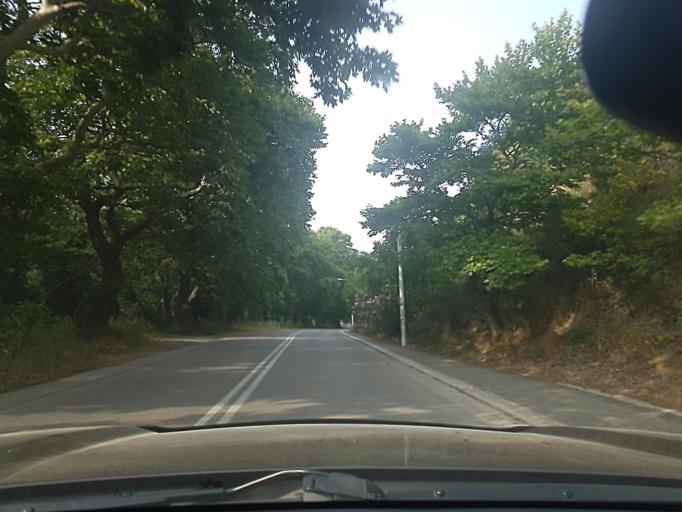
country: GR
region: Central Greece
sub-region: Nomos Evvoias
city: Yimnon
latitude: 38.5778
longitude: 23.8335
